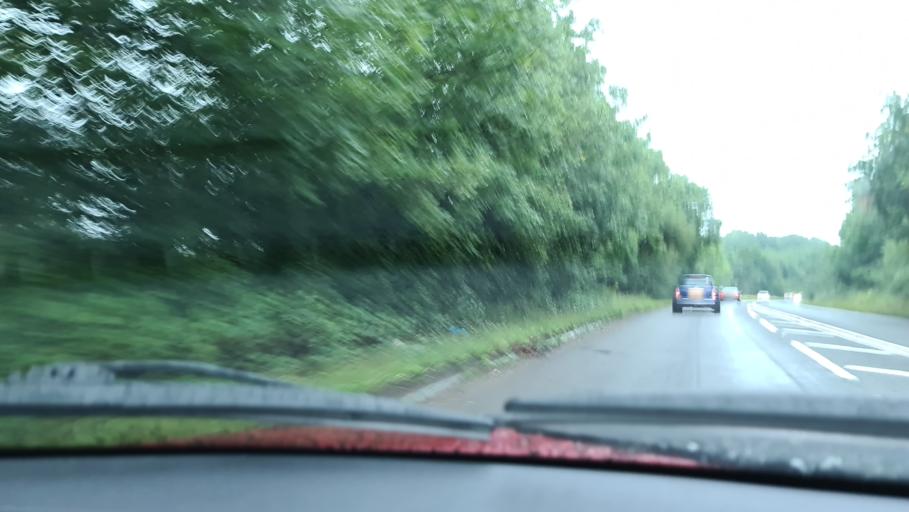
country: GB
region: England
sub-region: Buckinghamshire
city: Amersham
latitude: 51.6555
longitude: -0.6147
